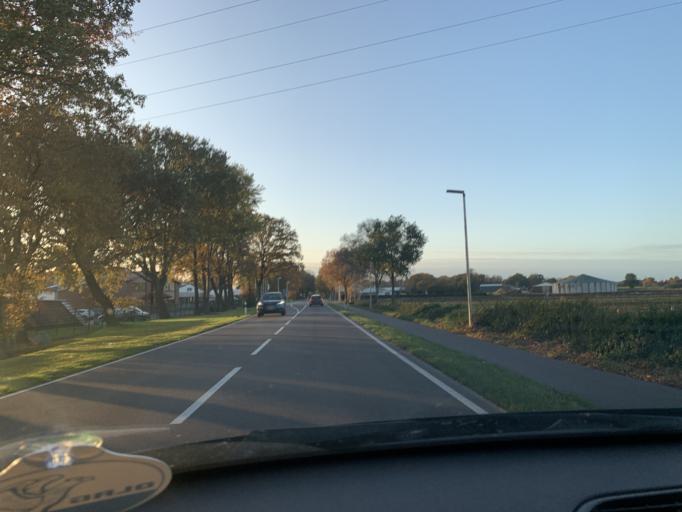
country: DE
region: Lower Saxony
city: Edewecht
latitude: 53.1237
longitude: 8.0063
